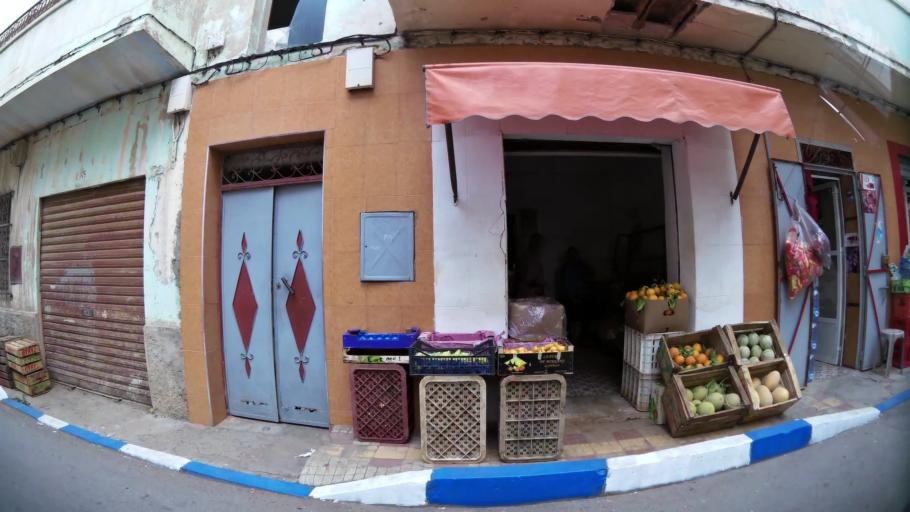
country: MA
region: Oriental
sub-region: Nador
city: Nador
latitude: 35.1718
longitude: -2.9308
